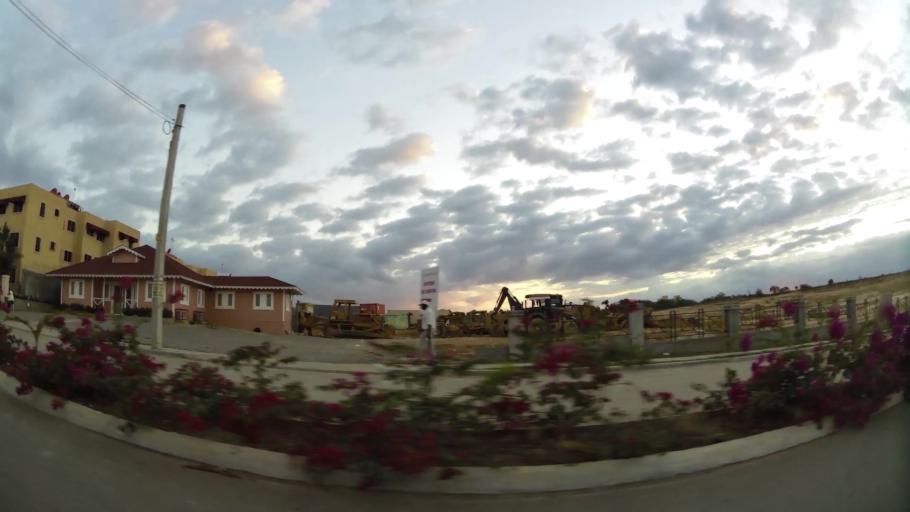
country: DO
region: Nacional
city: La Agustina
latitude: 18.5633
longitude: -69.9447
